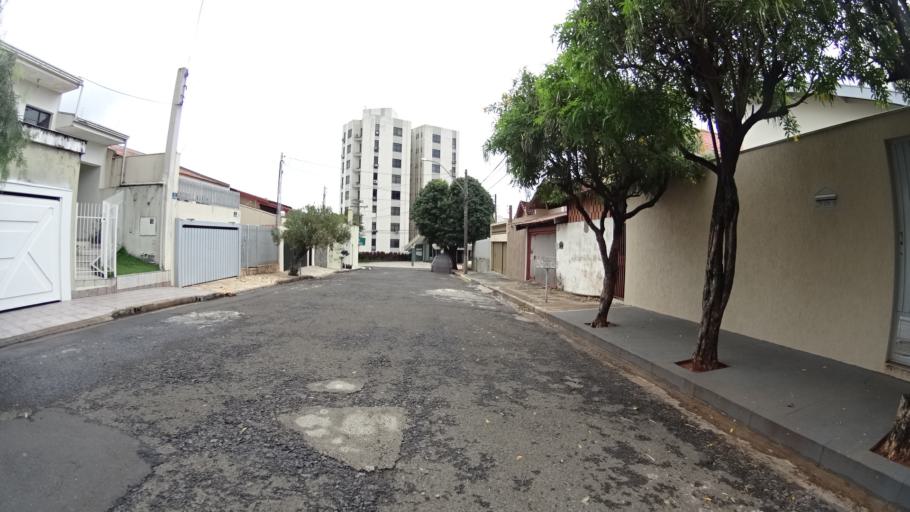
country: BR
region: Sao Paulo
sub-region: Marilia
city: Marilia
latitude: -22.2225
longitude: -49.9578
